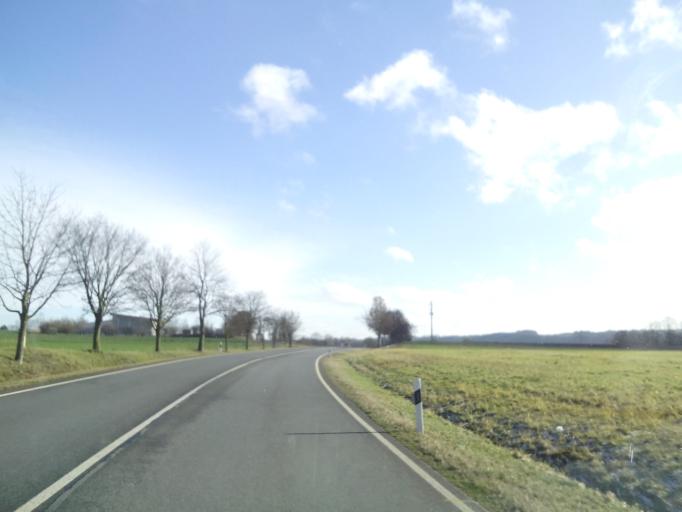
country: DE
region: Bavaria
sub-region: Upper Franconia
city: Mainleus
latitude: 50.1138
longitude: 11.3510
